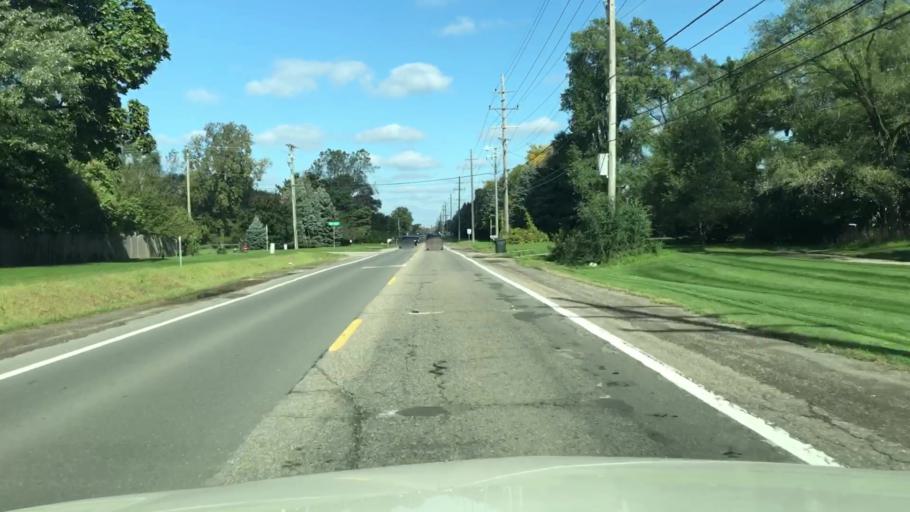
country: US
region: Michigan
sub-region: Oakland County
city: Rochester
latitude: 42.6489
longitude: -83.0926
